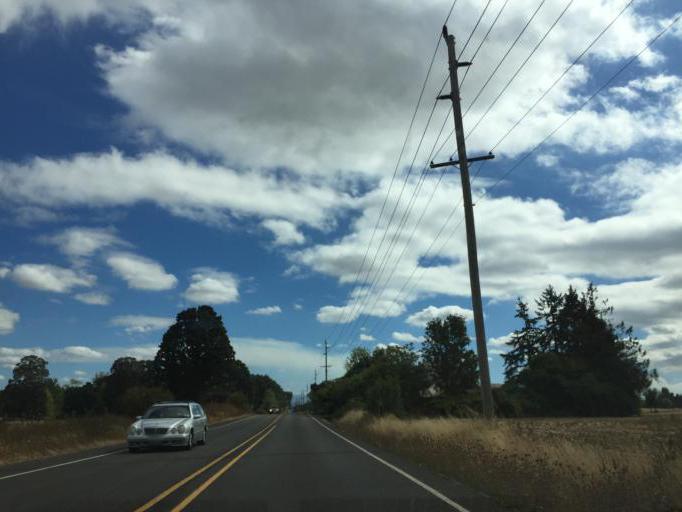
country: US
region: Oregon
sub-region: Marion County
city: Mount Angel
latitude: 45.1181
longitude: -122.7977
